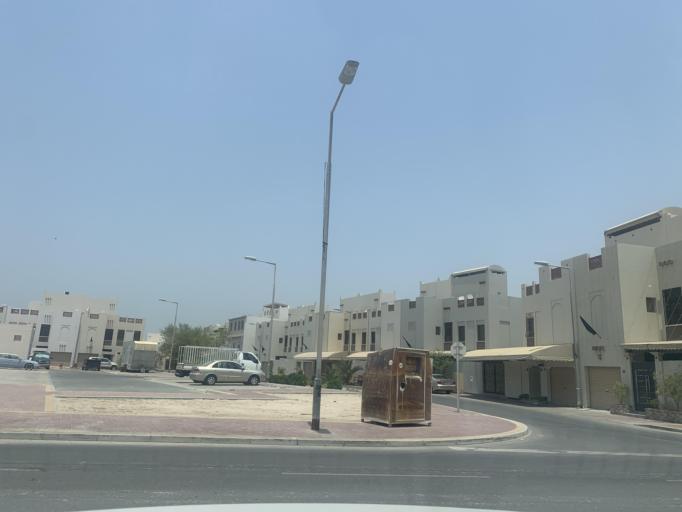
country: BH
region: Central Governorate
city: Madinat Hamad
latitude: 26.1448
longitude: 50.4623
